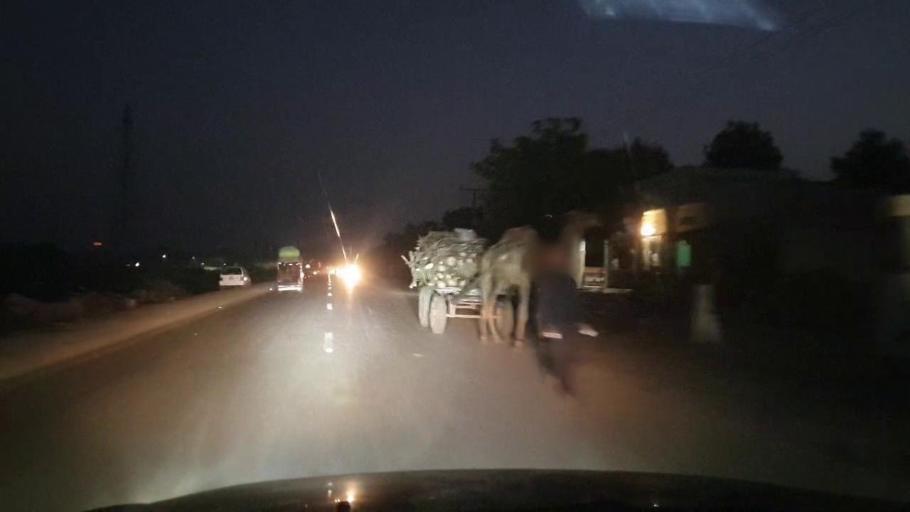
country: PK
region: Sindh
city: Chambar
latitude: 25.3021
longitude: 68.8098
